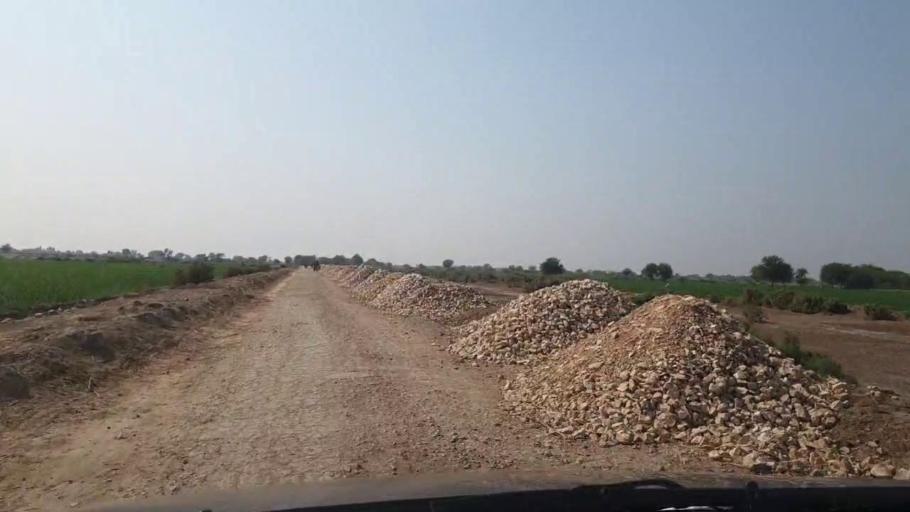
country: PK
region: Sindh
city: Jhol
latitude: 25.8887
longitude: 68.9995
